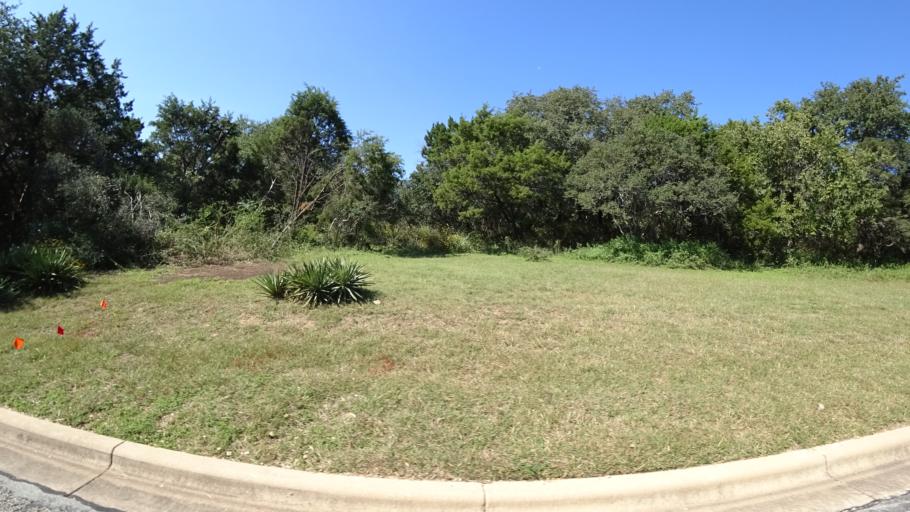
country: US
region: Texas
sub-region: Travis County
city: Rollingwood
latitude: 30.2750
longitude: -97.7972
